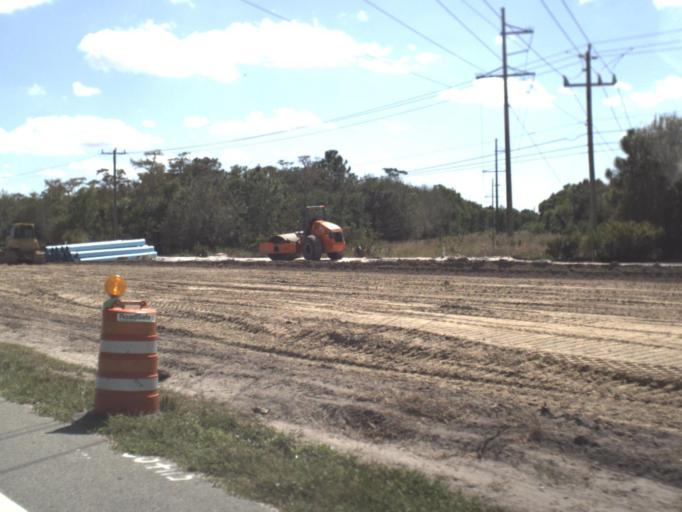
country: US
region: Florida
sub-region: Collier County
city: Lely Resort
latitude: 26.0536
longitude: -81.6839
